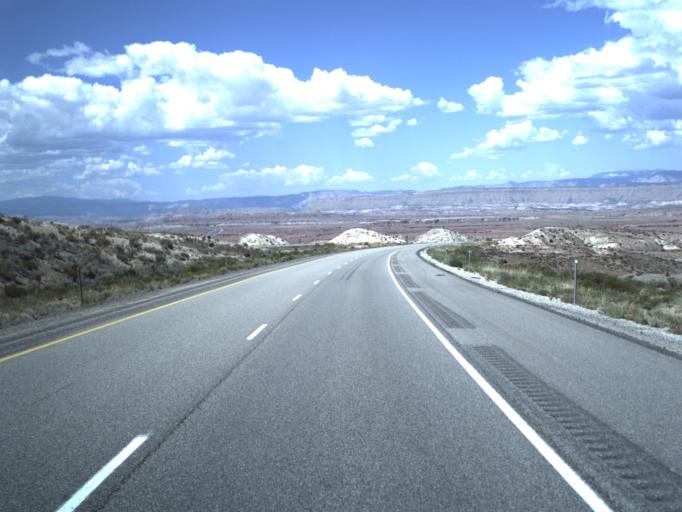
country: US
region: Utah
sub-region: Emery County
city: Ferron
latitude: 38.8442
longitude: -110.9814
